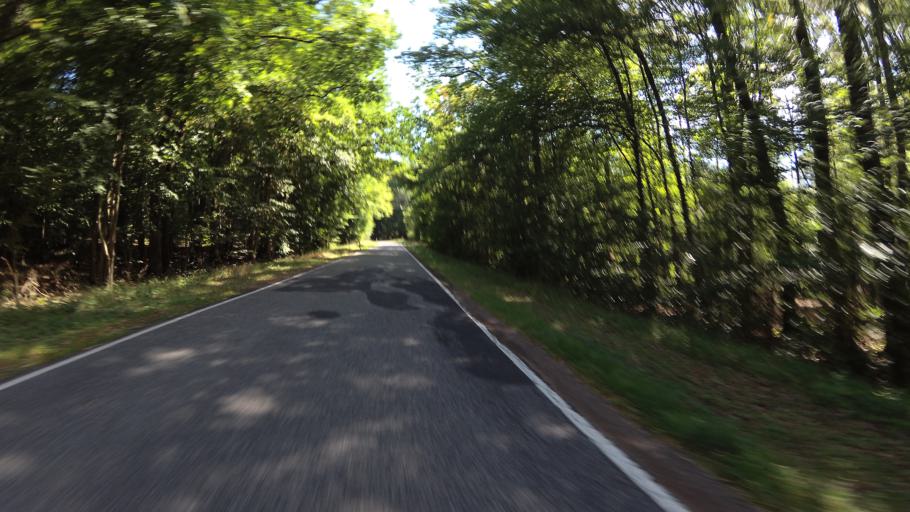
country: DE
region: Rheinland-Pfalz
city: Hornbach
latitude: 49.1558
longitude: 7.3231
